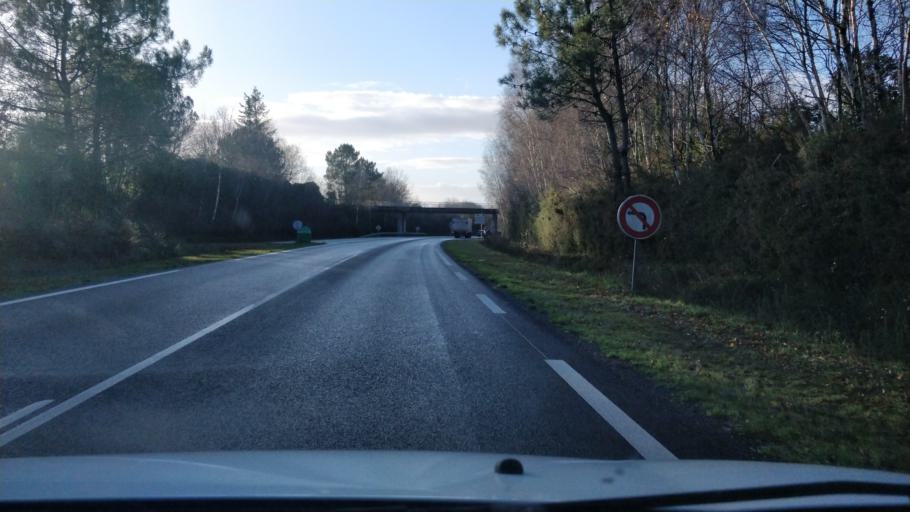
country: FR
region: Pays de la Loire
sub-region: Departement de la Loire-Atlantique
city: Fegreac
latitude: 47.5827
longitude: -2.0375
